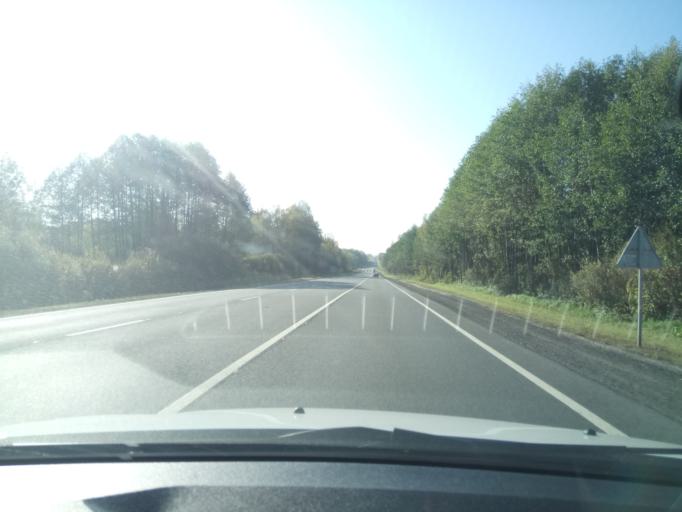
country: RU
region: Nizjnij Novgorod
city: Dal'neye Konstantinovo
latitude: 55.9868
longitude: 43.9703
